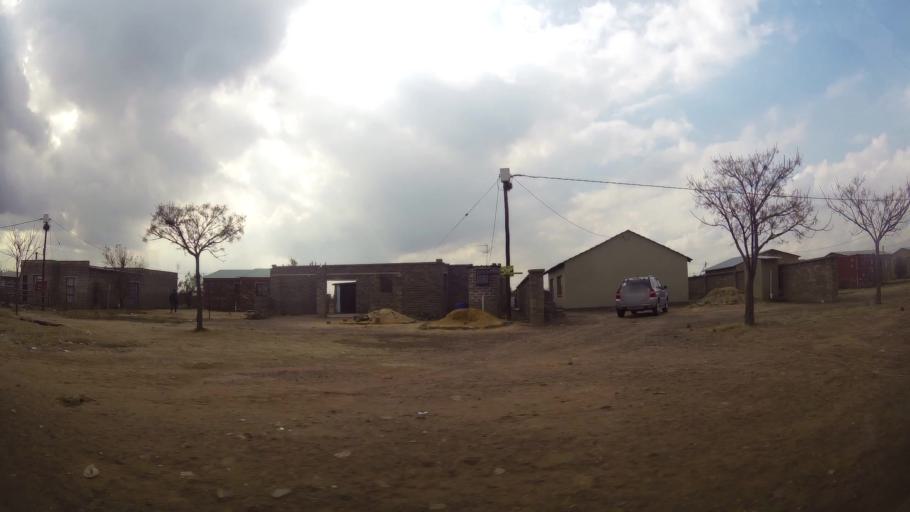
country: ZA
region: Orange Free State
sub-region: Fezile Dabi District Municipality
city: Sasolburg
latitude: -26.8564
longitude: 27.8911
